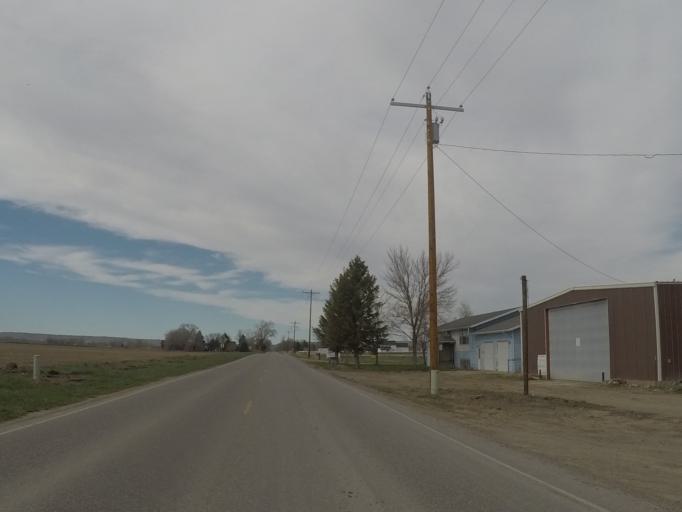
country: US
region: Montana
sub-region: Yellowstone County
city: Laurel
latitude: 45.7192
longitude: -108.6587
